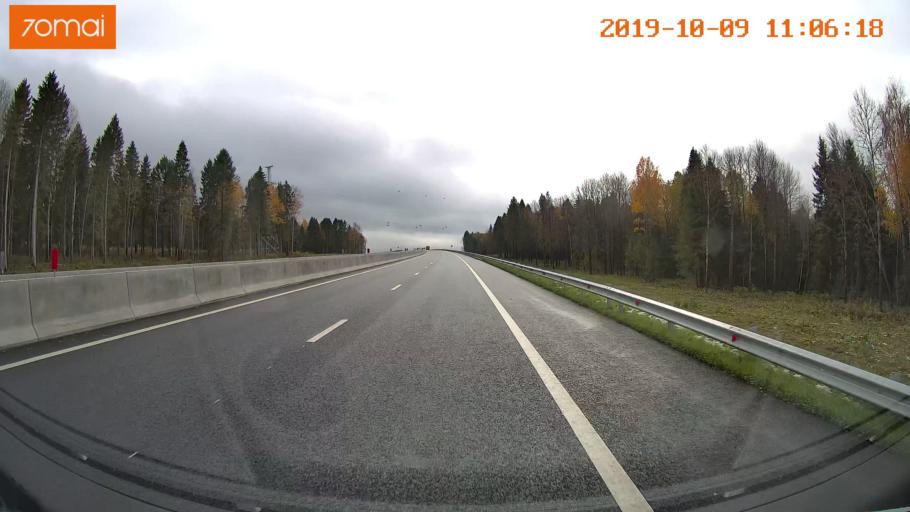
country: RU
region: Vologda
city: Vologda
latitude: 59.1884
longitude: 39.7595
